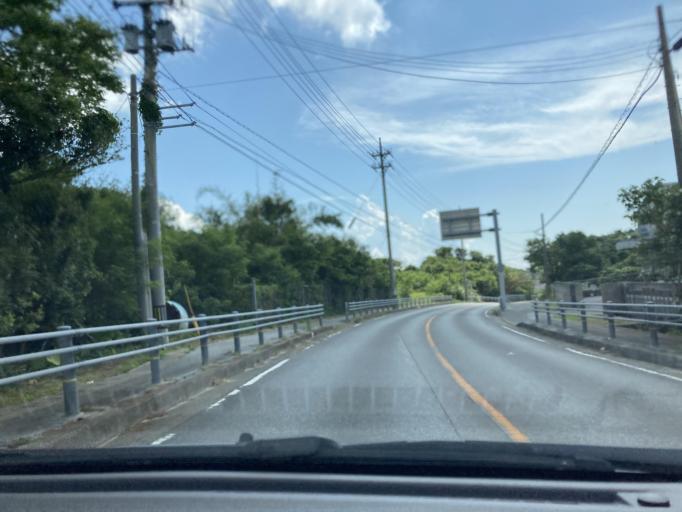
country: JP
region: Okinawa
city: Tomigusuku
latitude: 26.1523
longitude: 127.7902
